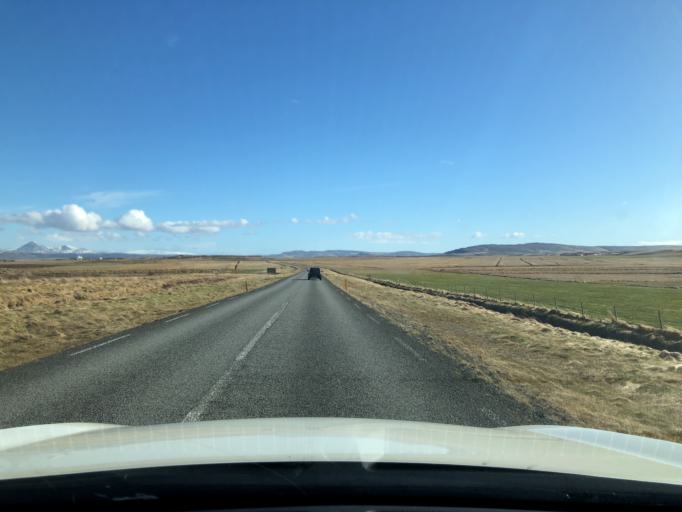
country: IS
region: West
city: Borgarnes
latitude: 64.5991
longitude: -21.5665
